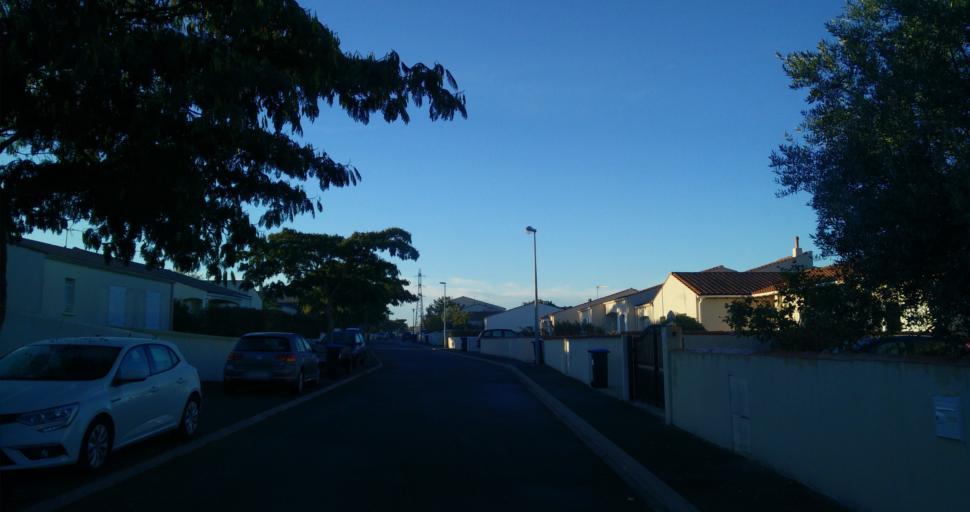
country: FR
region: Poitou-Charentes
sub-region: Departement de la Charente-Maritime
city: Puilboreau
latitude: 46.1862
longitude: -1.1259
